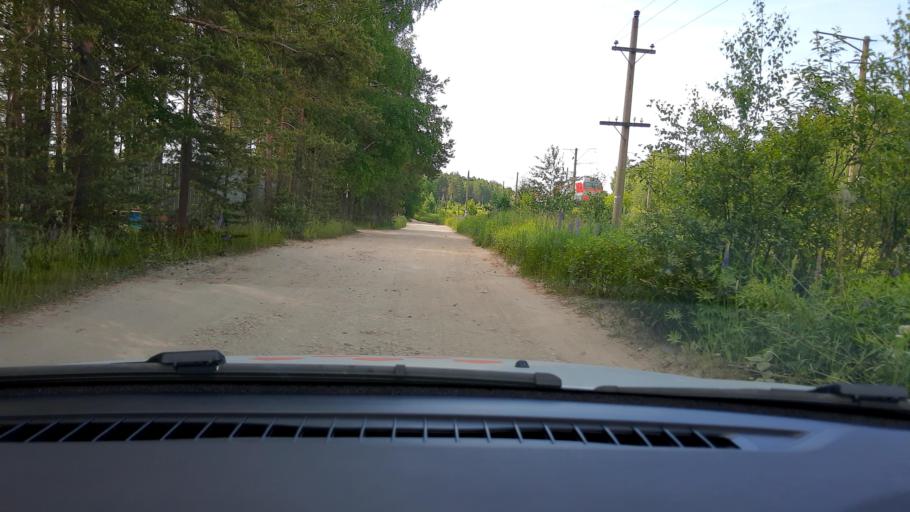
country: RU
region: Nizjnij Novgorod
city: Linda
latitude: 56.6638
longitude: 44.1686
